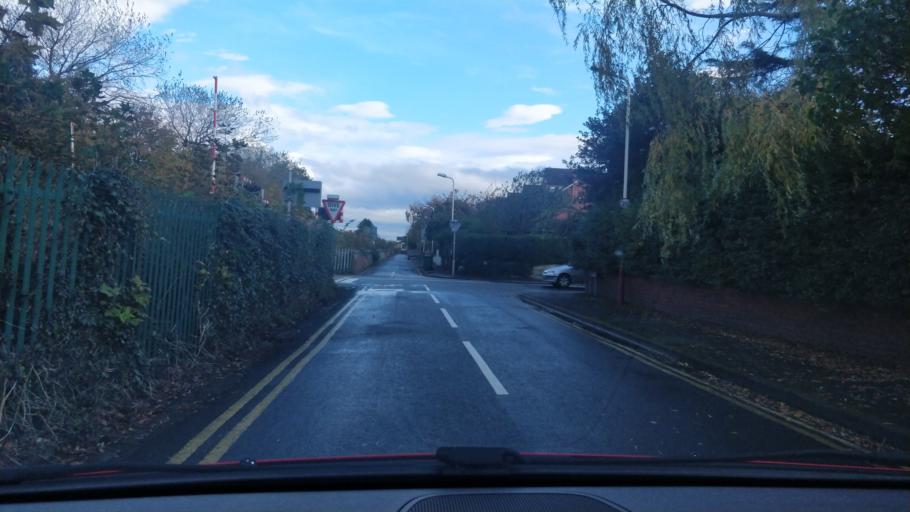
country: GB
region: England
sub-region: Sefton
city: Southport
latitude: 53.6291
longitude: -3.0186
